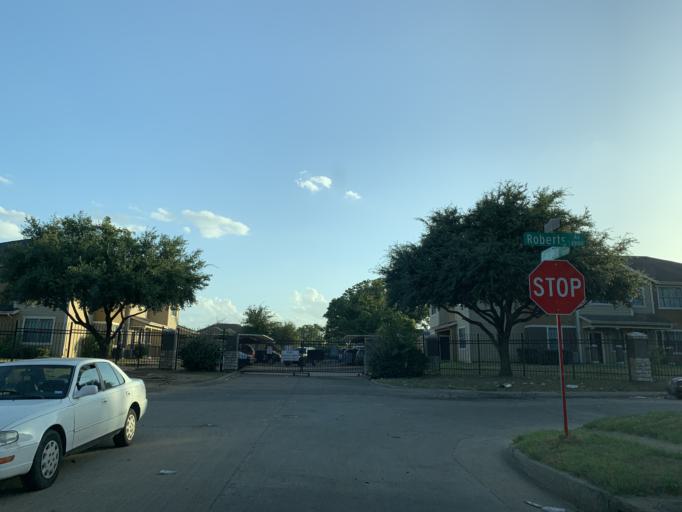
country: US
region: Texas
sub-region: Dallas County
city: Dallas
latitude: 32.7579
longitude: -96.7462
